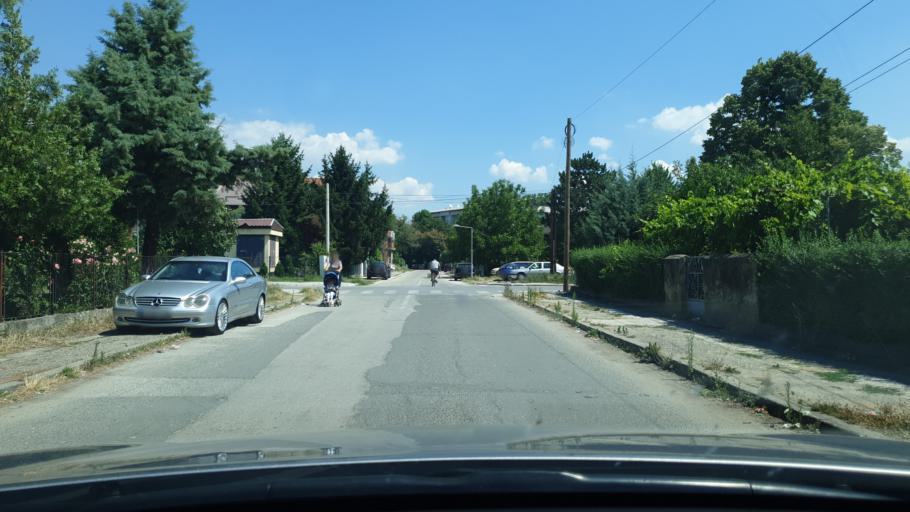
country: MK
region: Kisela Voda
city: Kisela Voda
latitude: 41.9416
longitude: 21.5171
